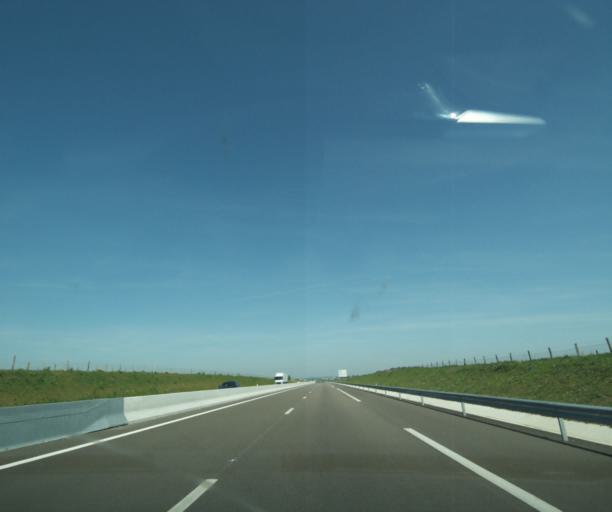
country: FR
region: Bourgogne
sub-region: Departement de la Nievre
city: Saint-Pierre-le-Moutier
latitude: 46.8079
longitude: 3.1212
